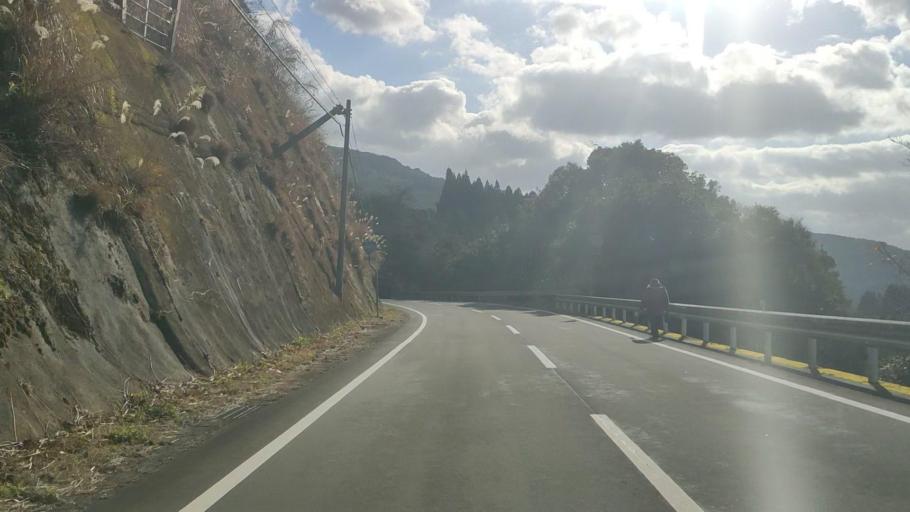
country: JP
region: Kumamoto
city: Hitoyoshi
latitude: 32.3193
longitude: 130.8423
